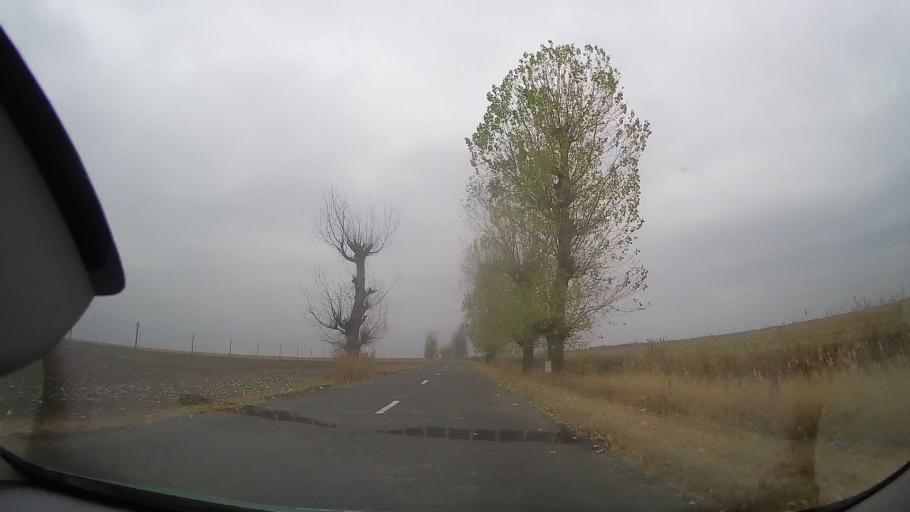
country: RO
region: Ialomita
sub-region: Comuna Grindu
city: Grindu
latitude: 44.7961
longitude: 26.8887
